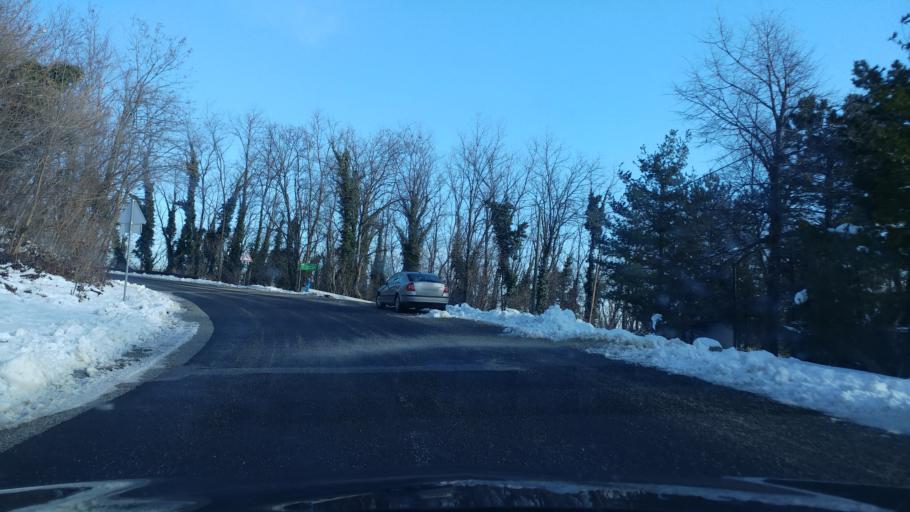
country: HR
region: Grad Zagreb
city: Stenjevec
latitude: 45.8415
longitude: 15.8897
